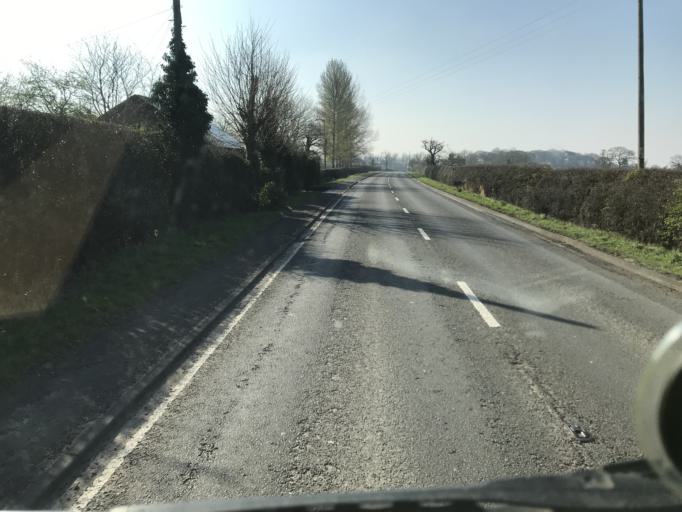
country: GB
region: England
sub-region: Cheshire West and Chester
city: Waverton
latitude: 53.1497
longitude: -2.8116
